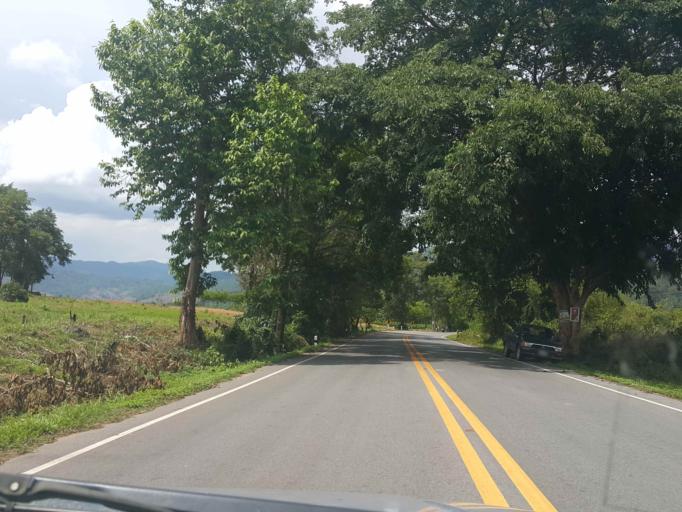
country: TH
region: Nan
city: Ban Luang
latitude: 18.8630
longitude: 100.4640
